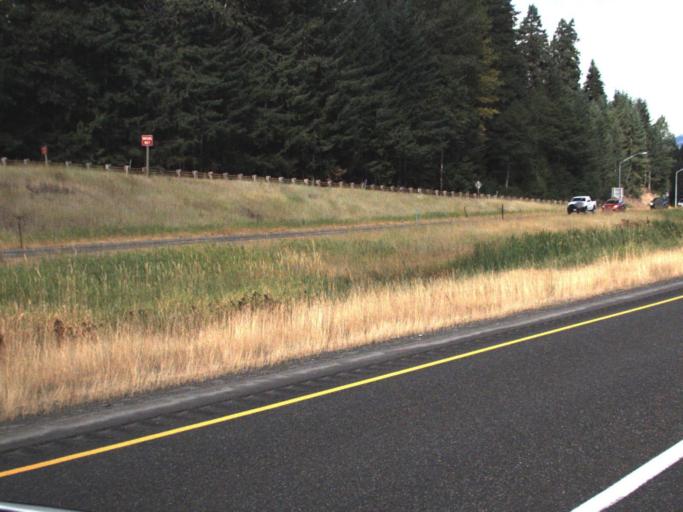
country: US
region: Washington
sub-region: Kittitas County
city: Cle Elum
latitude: 47.2979
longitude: -121.2887
